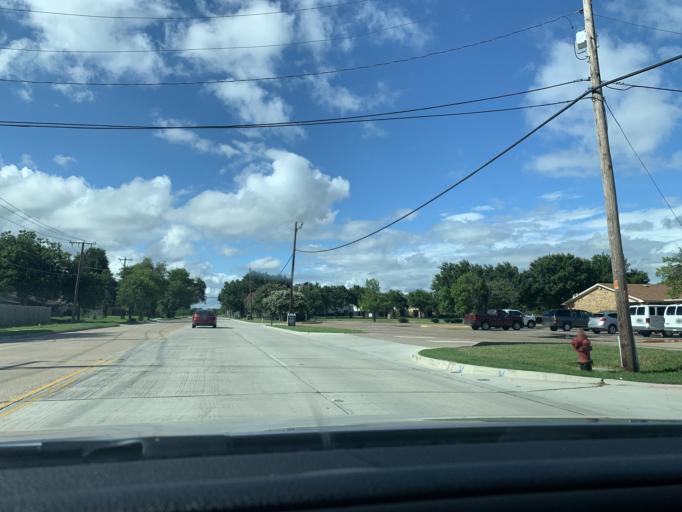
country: US
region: Texas
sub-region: Dallas County
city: Grand Prairie
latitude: 32.6594
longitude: -97.0278
